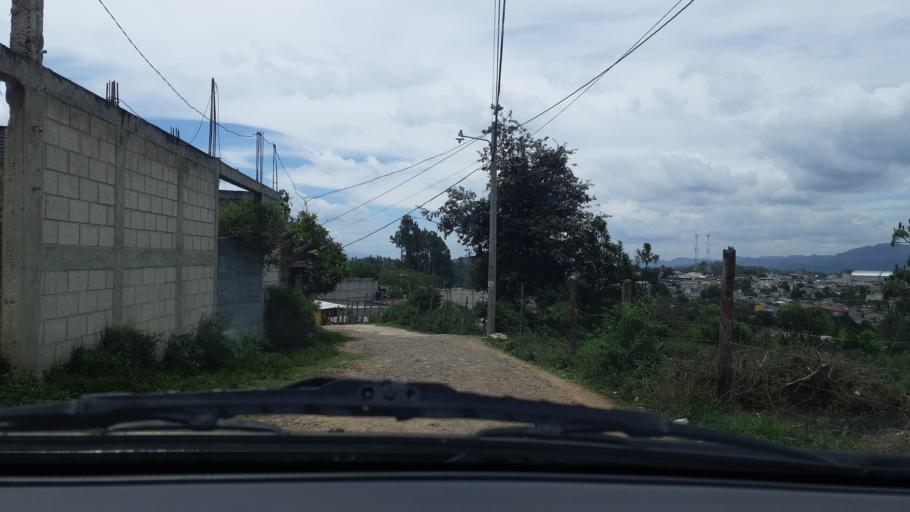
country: GT
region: Chimaltenango
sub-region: Municipio de Chimaltenango
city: Chimaltenango
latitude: 14.6627
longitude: -90.8509
